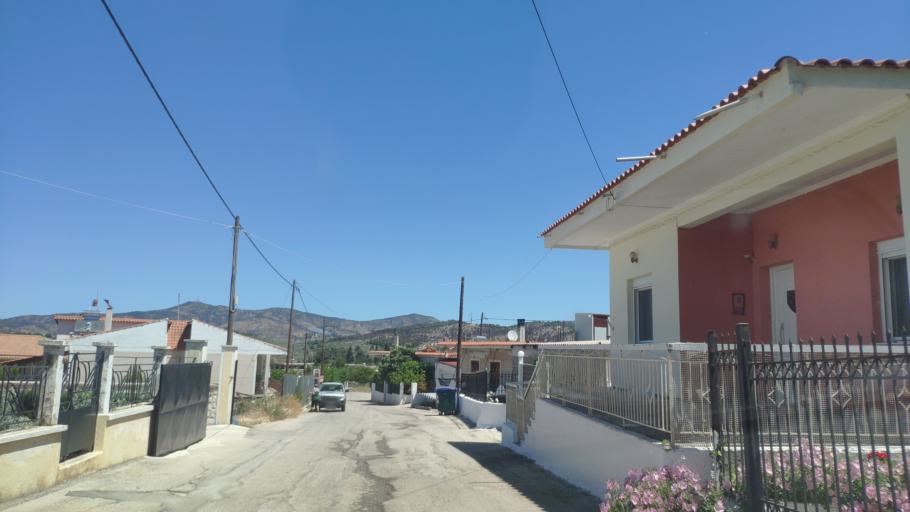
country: GR
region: Peloponnese
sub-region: Nomos Korinthias
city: Athikia
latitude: 37.8159
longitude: 22.9238
